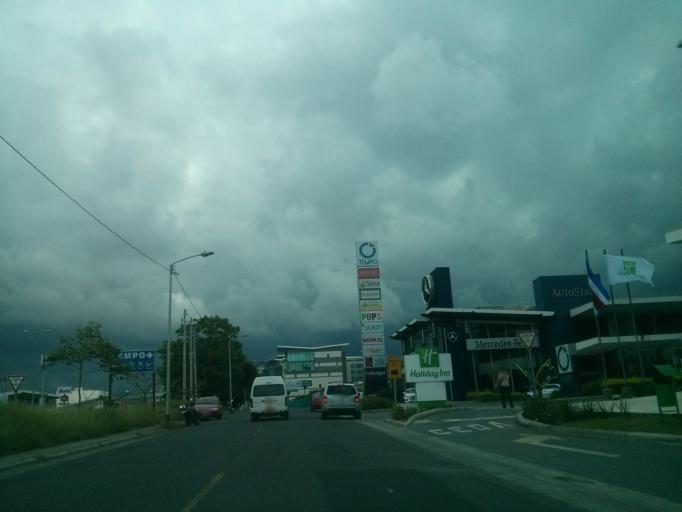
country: CR
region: San Jose
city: San Rafael
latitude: 9.9422
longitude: -84.1464
